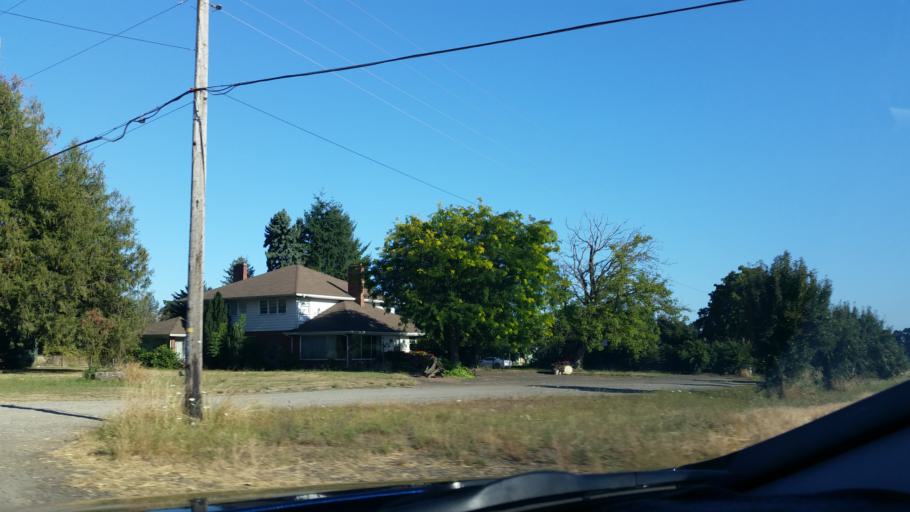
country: US
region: Oregon
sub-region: Marion County
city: Hubbard
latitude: 45.2306
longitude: -122.8283
